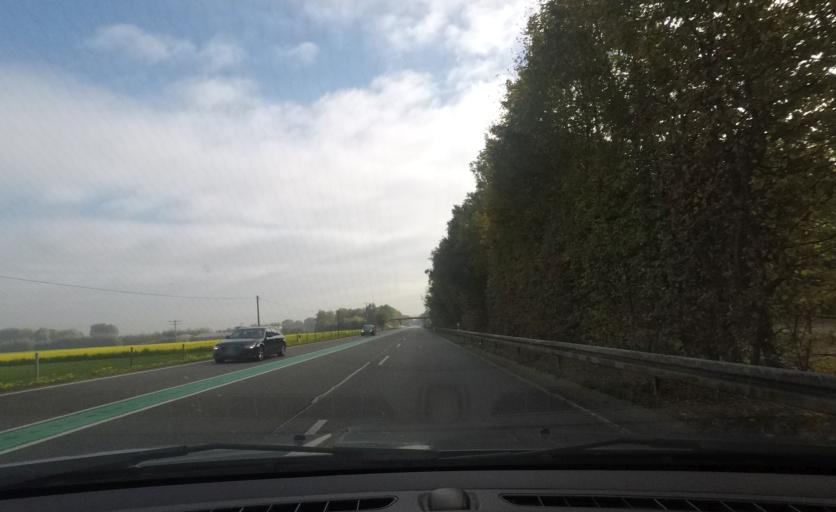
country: DE
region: North Rhine-Westphalia
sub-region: Regierungsbezirk Munster
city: Velen
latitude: 51.8530
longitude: 7.0166
